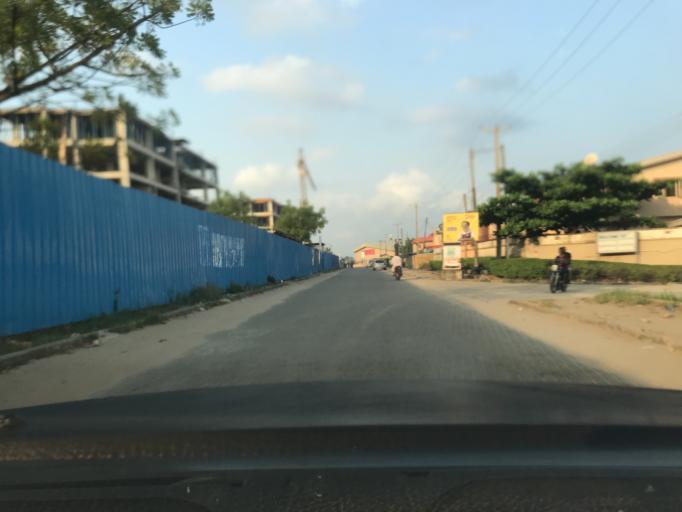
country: NG
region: Lagos
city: Festac Town
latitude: 6.4648
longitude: 3.3069
